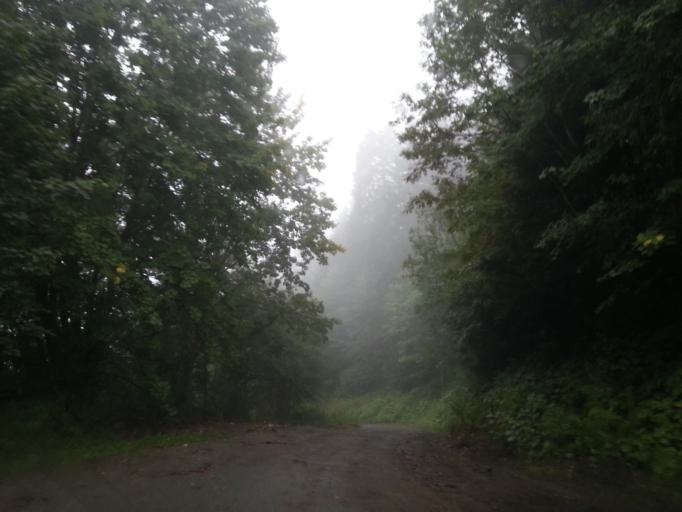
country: FR
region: Rhone-Alpes
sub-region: Departement de la Savoie
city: Marthod
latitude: 45.7032
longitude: 6.4592
